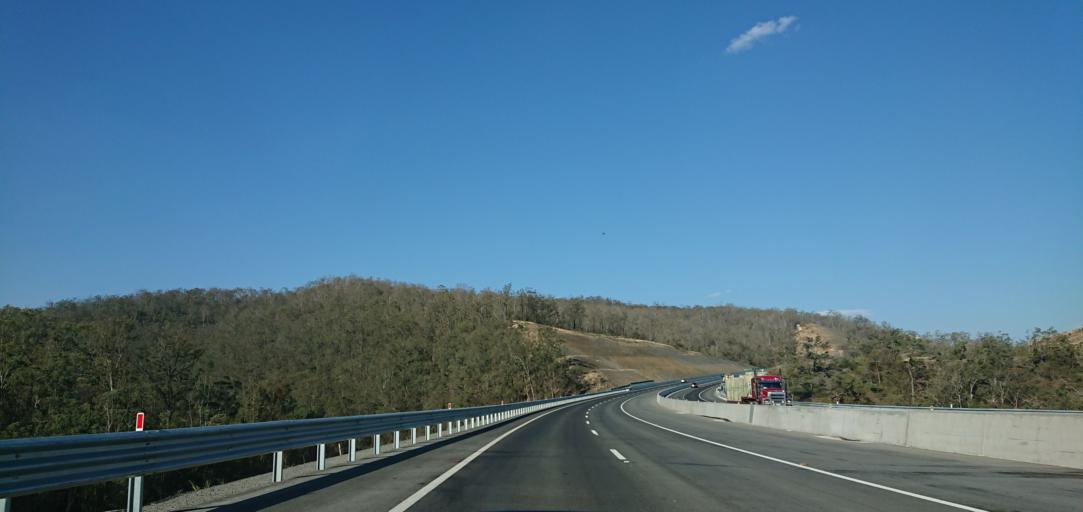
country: AU
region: Queensland
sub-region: Toowoomba
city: Wilsonton Heights
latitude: -27.4985
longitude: 151.9790
